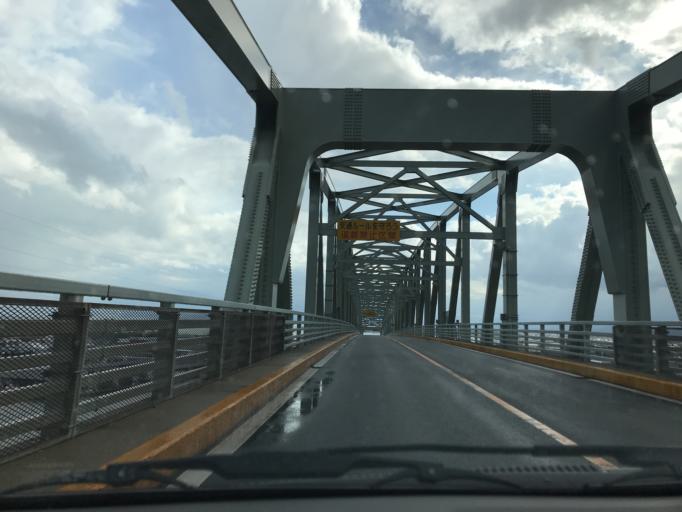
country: JP
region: Shimane
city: Sakaiminato
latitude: 35.5505
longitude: 133.2440
